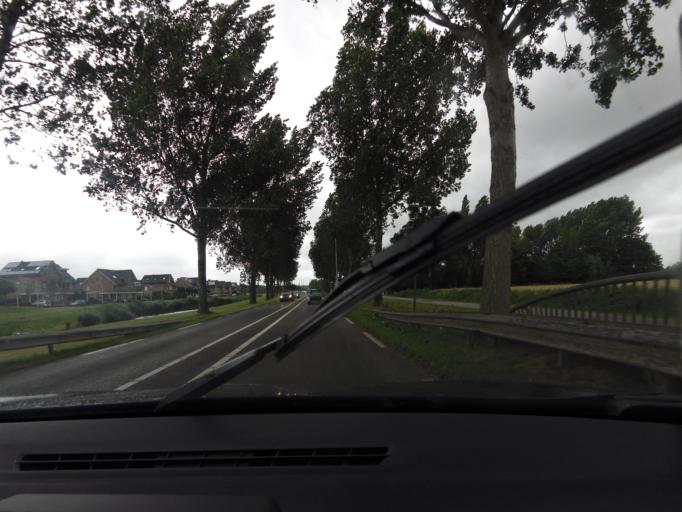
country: NL
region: South Holland
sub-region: Gemeente Hellevoetsluis
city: Nieuwenhoorn
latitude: 51.8496
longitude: 4.1647
